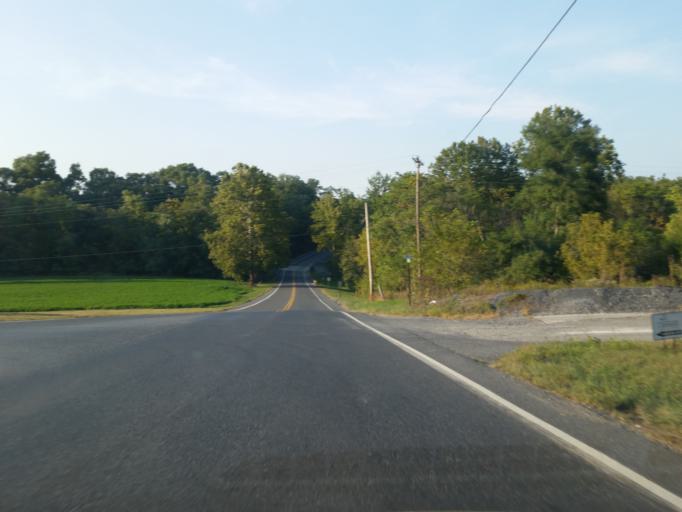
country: US
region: Pennsylvania
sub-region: Lebanon County
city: Annville
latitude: 40.3309
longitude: -76.5413
